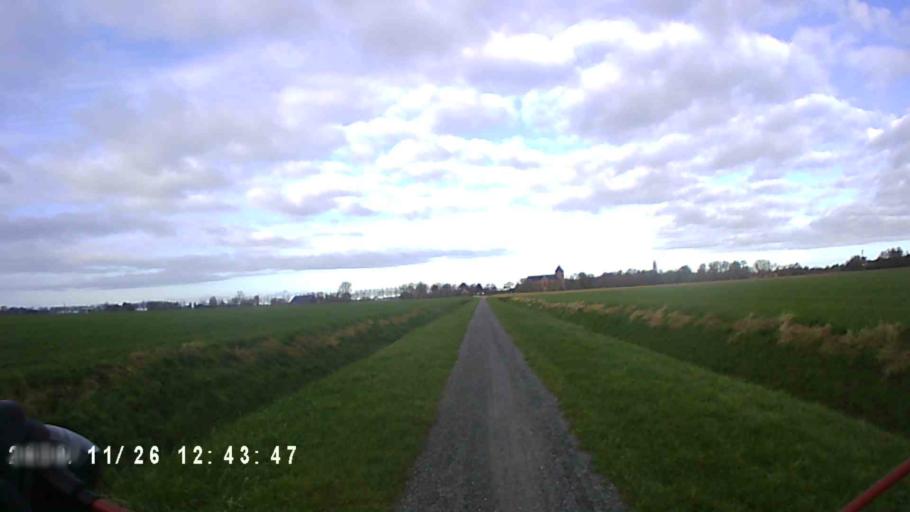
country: NL
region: Groningen
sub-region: Gemeente Appingedam
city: Appingedam
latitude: 53.3402
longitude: 6.7624
